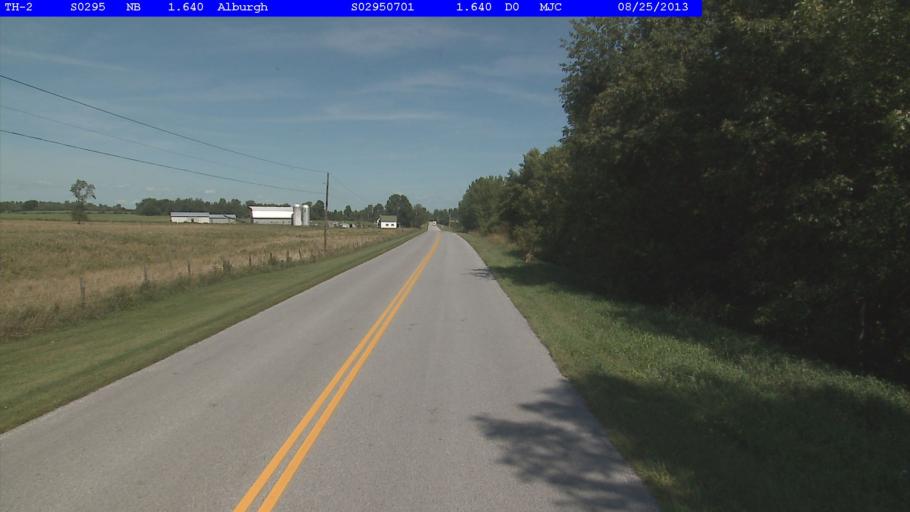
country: US
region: Vermont
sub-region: Franklin County
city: Swanton
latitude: 44.9965
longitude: -73.2200
